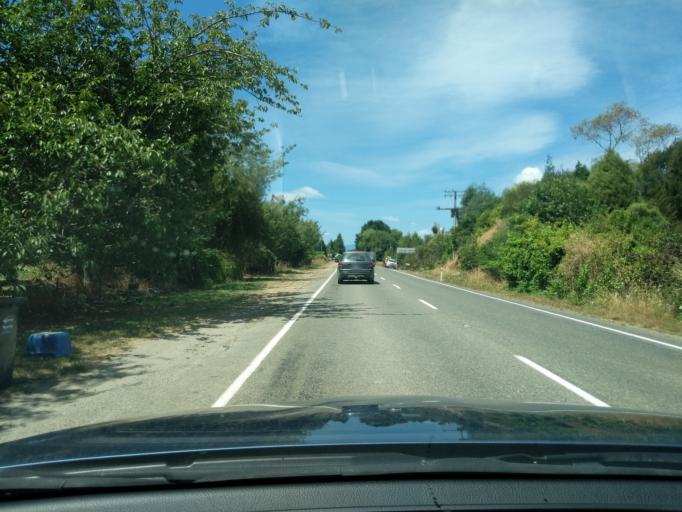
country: NZ
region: Tasman
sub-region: Tasman District
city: Motueka
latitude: -41.0582
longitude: 172.9686
